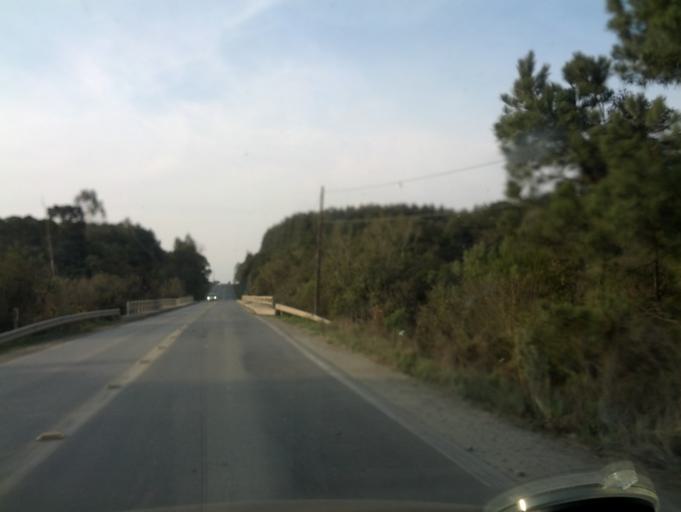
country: BR
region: Santa Catarina
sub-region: Otacilio Costa
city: Otacilio Costa
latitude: -27.5162
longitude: -50.1329
